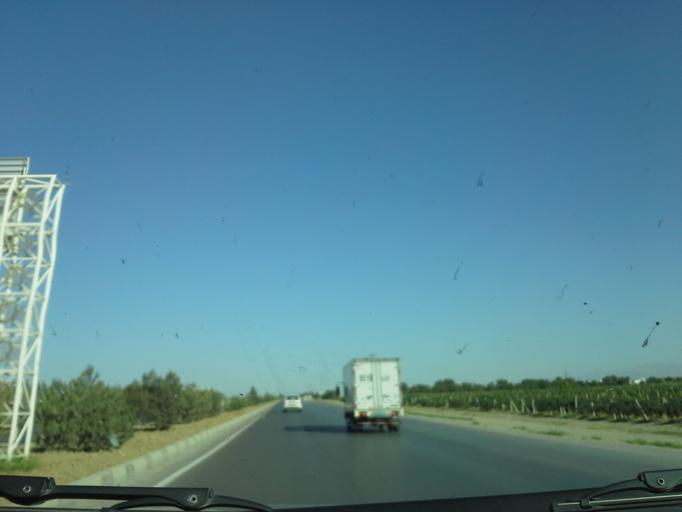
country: TM
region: Ahal
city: Abadan
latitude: 38.0855
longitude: 58.1175
